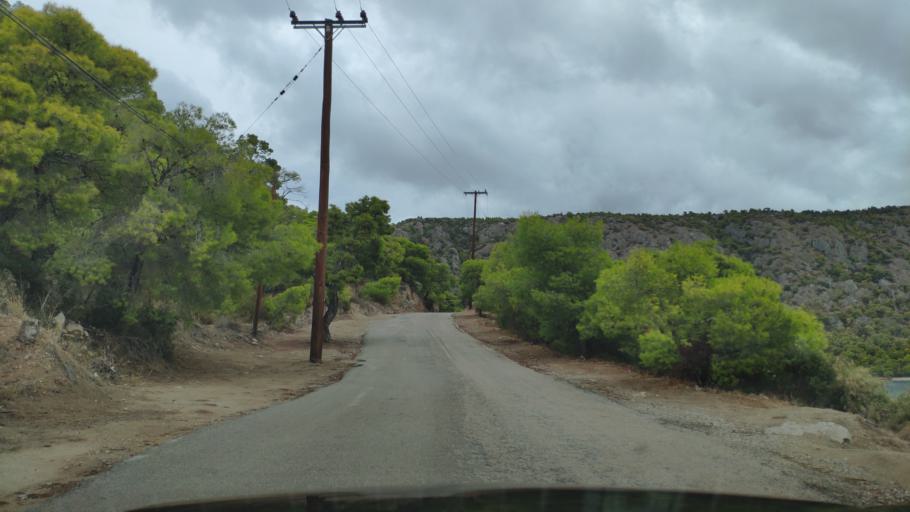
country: GR
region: Peloponnese
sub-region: Nomos Korinthias
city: Perachora
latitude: 38.0287
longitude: 22.8716
